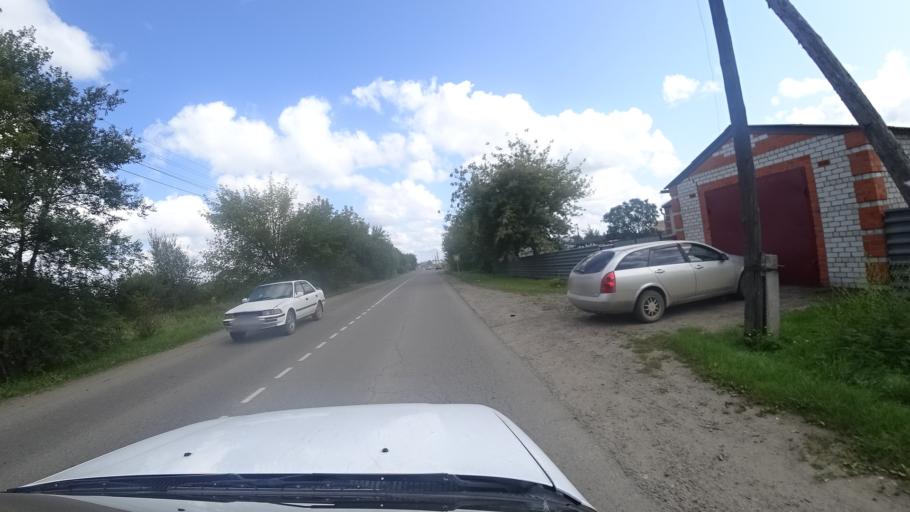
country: RU
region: Primorskiy
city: Dal'nerechensk
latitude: 45.9258
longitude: 133.7699
